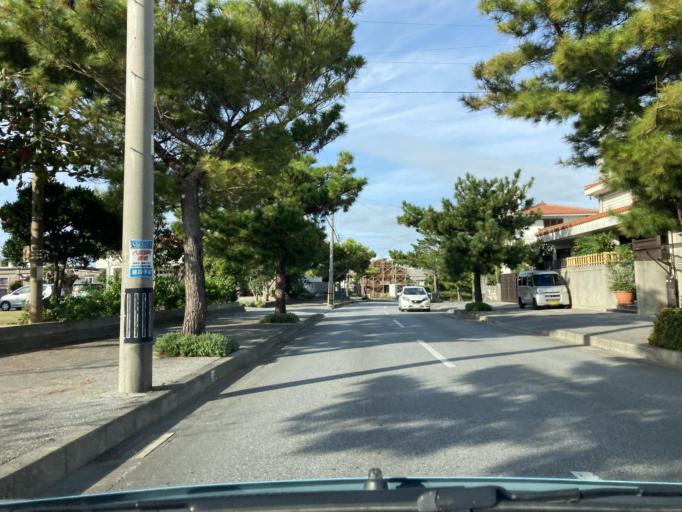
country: JP
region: Okinawa
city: Itoman
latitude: 26.1391
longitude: 127.7435
